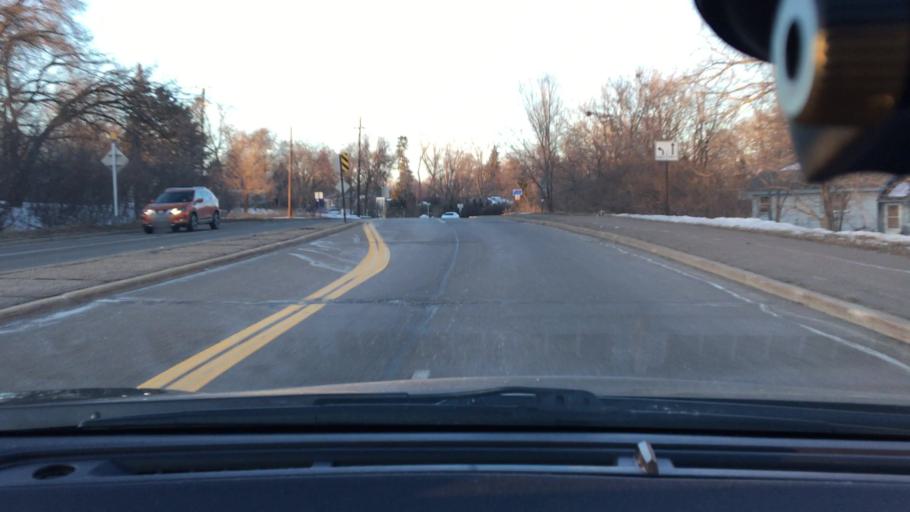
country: US
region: Minnesota
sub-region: Hennepin County
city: Minnetonka Mills
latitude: 44.9469
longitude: -93.3991
